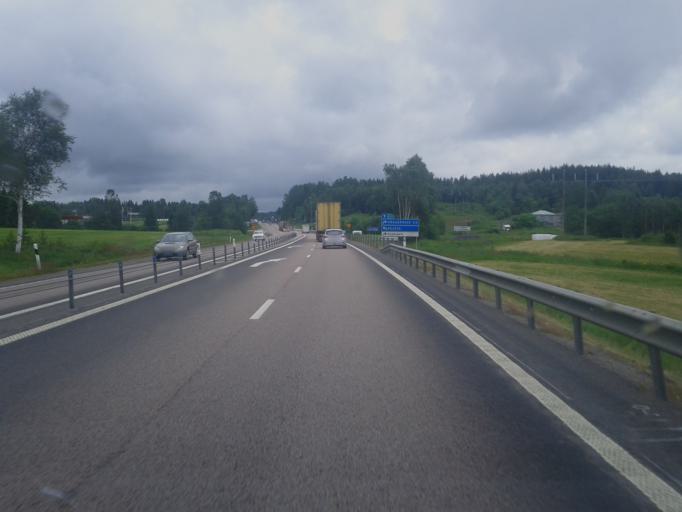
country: SE
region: Vaesternorrland
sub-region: Haernoesands Kommun
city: Haernoesand
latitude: 62.5866
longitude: 17.7841
